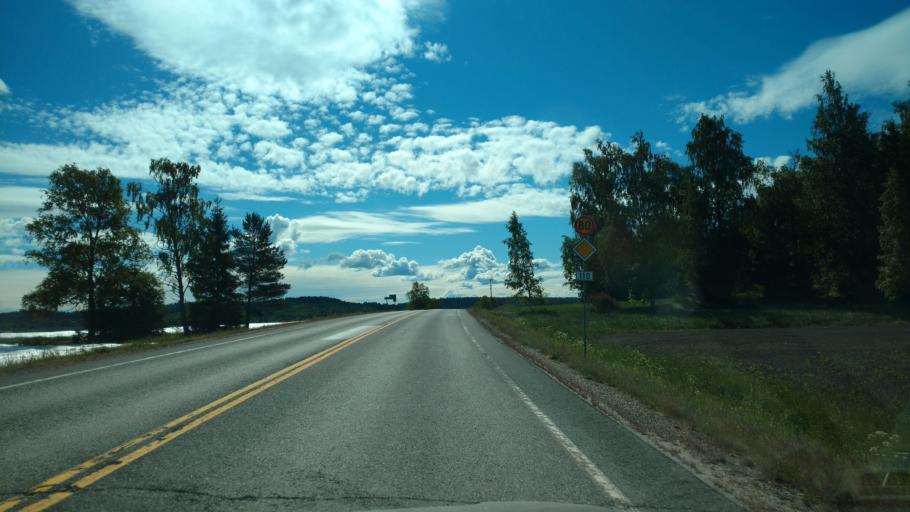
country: FI
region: Varsinais-Suomi
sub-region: Salo
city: Muurla
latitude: 60.3822
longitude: 23.2933
